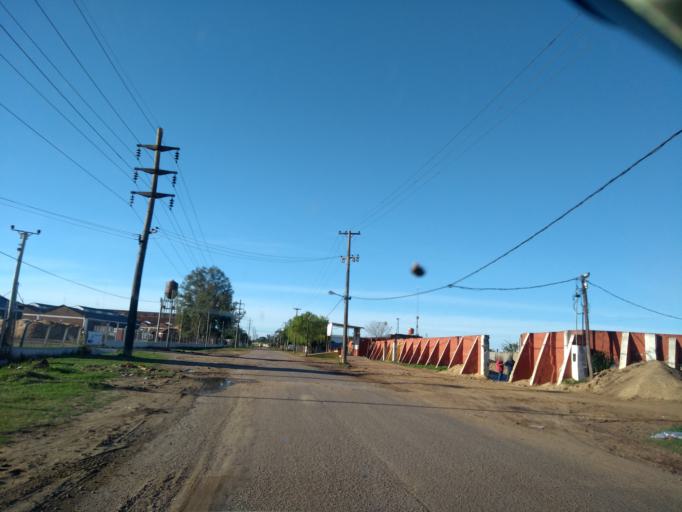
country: AR
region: Chaco
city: Barranqueras
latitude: -27.4977
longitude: -58.9317
